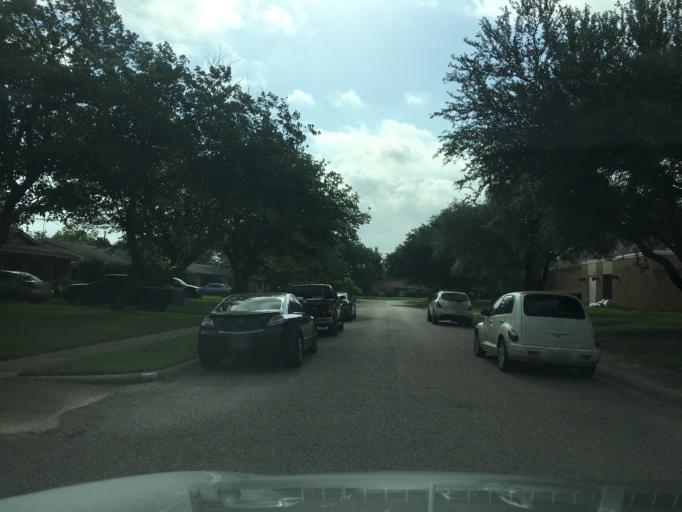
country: US
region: Texas
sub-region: Dallas County
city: Richardson
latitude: 32.9493
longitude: -96.7175
